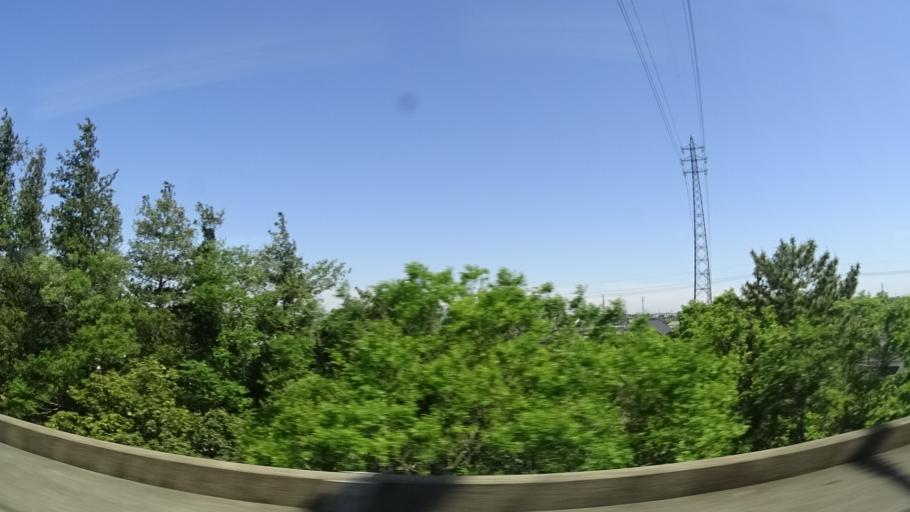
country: JP
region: Saitama
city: Kukichuo
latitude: 36.0788
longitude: 139.6861
